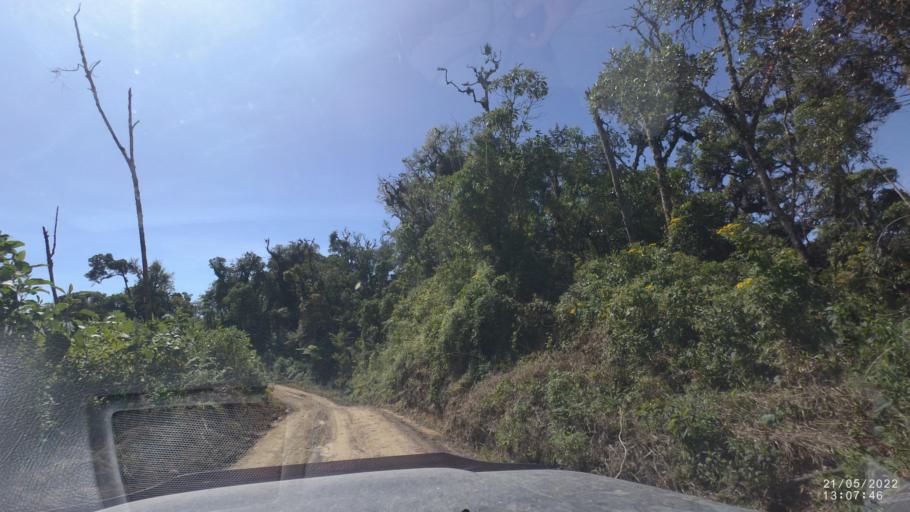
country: BO
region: Cochabamba
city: Colomi
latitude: -17.1499
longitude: -65.9442
